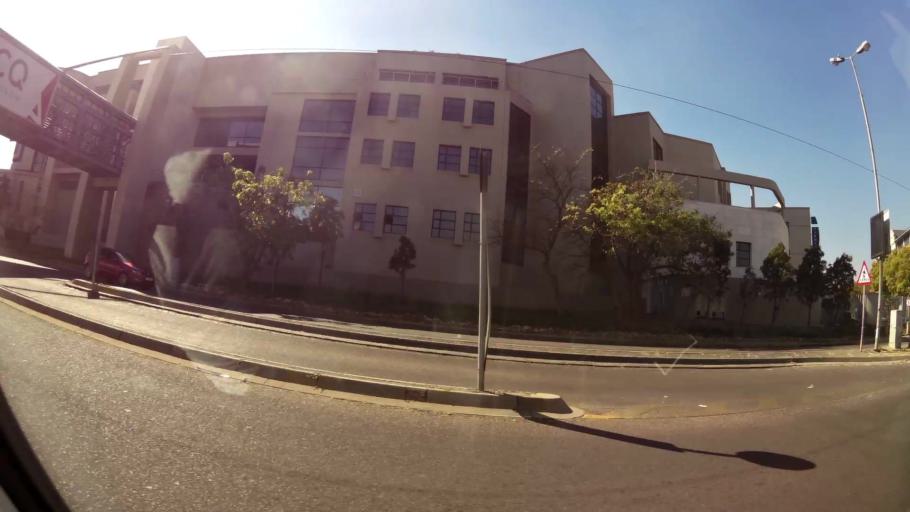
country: ZA
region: Gauteng
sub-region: City of Tshwane Metropolitan Municipality
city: Pretoria
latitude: -25.7712
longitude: 28.2356
